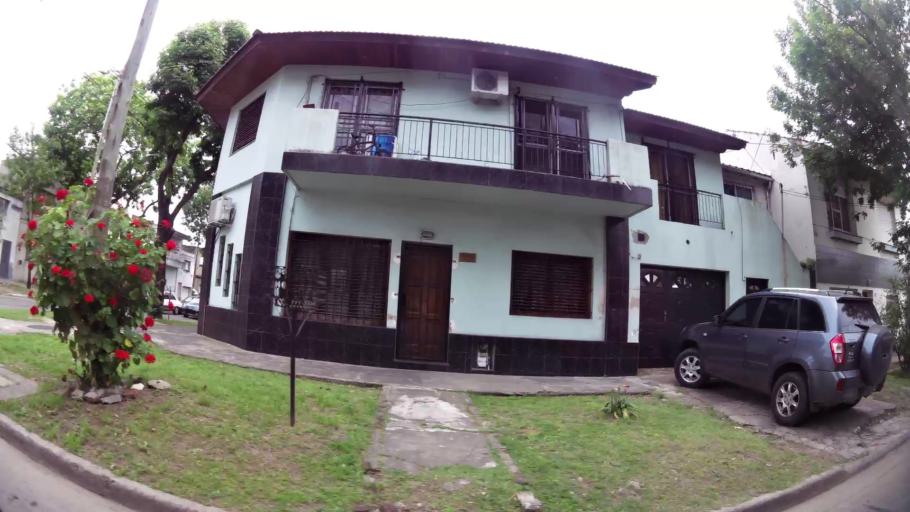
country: AR
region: Buenos Aires
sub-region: Partido de Avellaneda
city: Avellaneda
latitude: -34.6786
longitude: -58.3744
